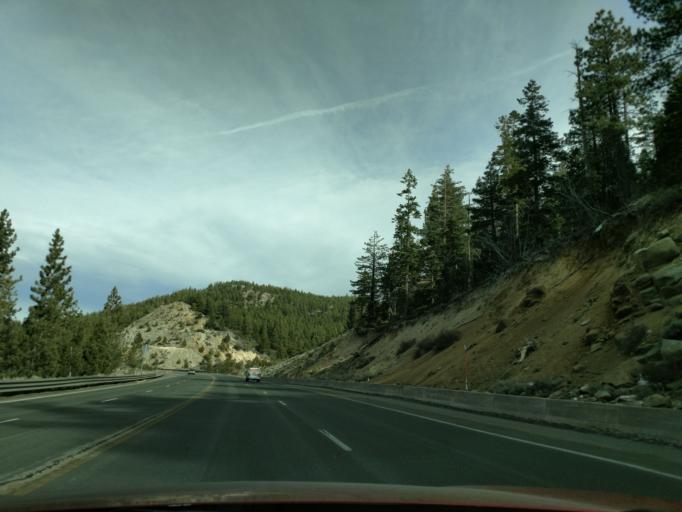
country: US
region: Nevada
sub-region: Douglas County
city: Kingsbury
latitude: 39.0873
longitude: -119.9137
